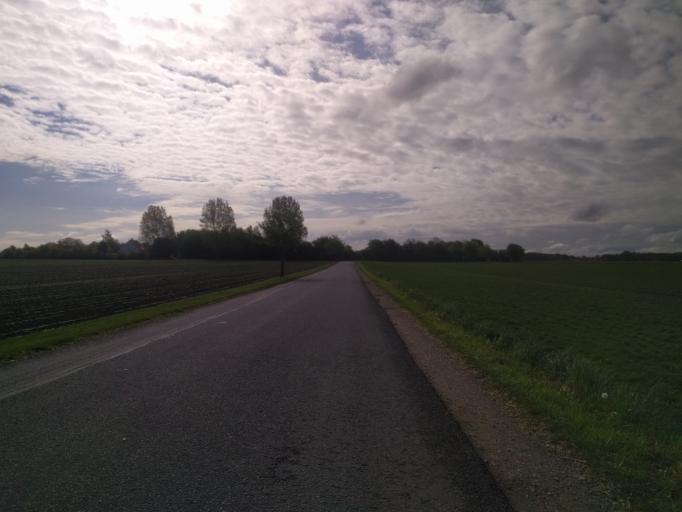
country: DK
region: South Denmark
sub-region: Kerteminde Kommune
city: Kerteminde
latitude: 55.4240
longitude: 10.6415
